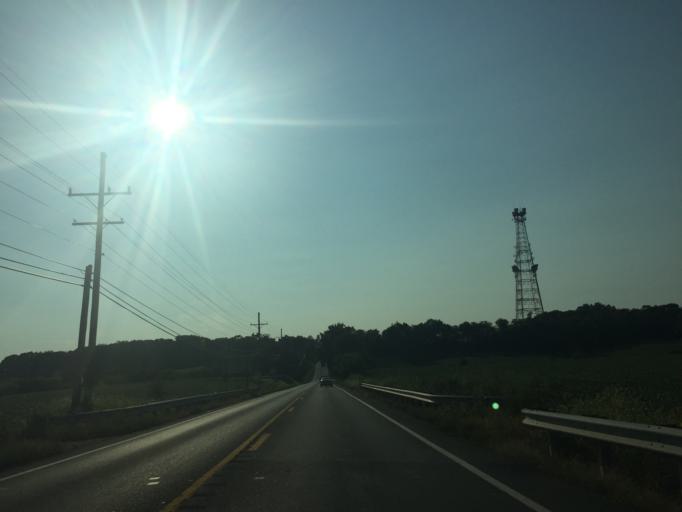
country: US
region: Maryland
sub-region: Frederick County
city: Green Valley
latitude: 39.3473
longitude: -77.2754
